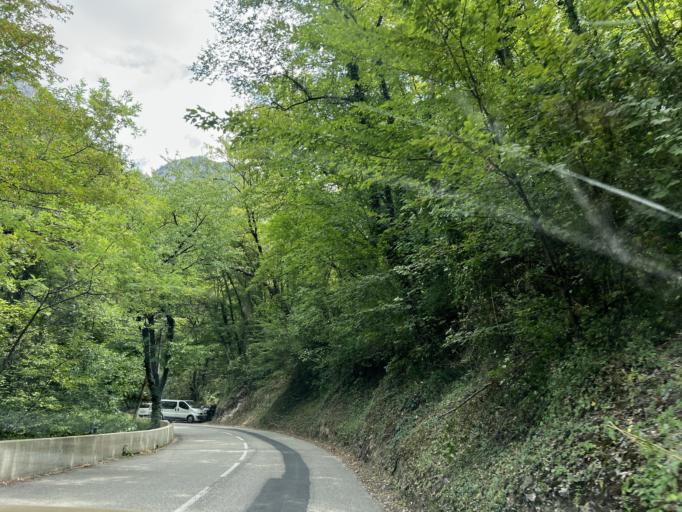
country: FR
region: Provence-Alpes-Cote d'Azur
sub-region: Departement des Alpes-Maritimes
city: Le Rouret
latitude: 43.7202
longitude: 6.9938
